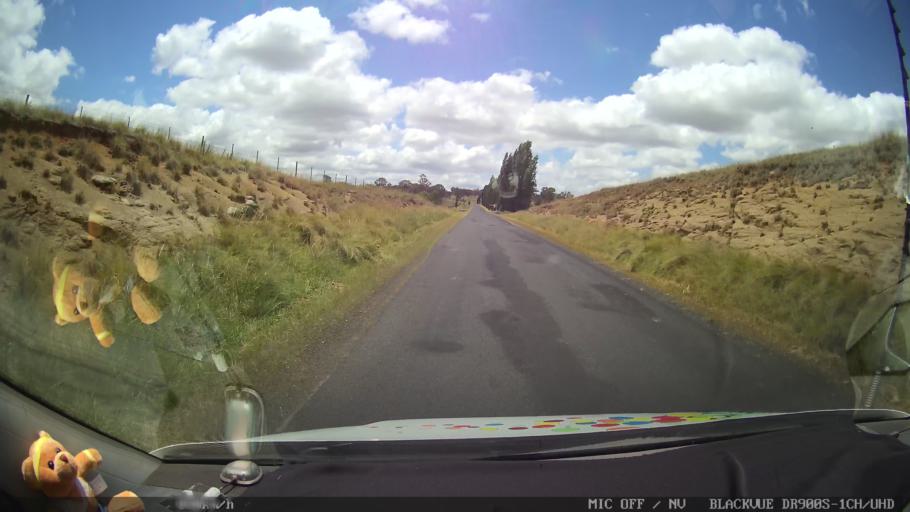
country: AU
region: New South Wales
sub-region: Glen Innes Severn
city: Glen Innes
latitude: -29.4372
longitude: 151.7608
